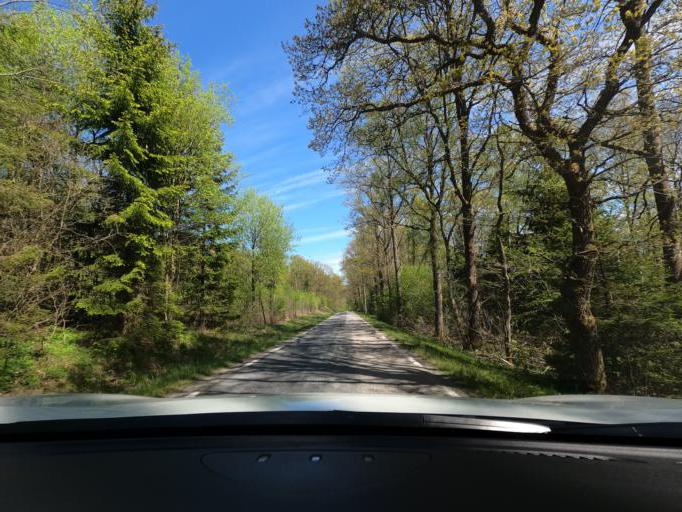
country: SE
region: Vaestra Goetaland
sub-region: Marks Kommun
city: Horred
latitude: 57.4339
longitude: 12.4142
